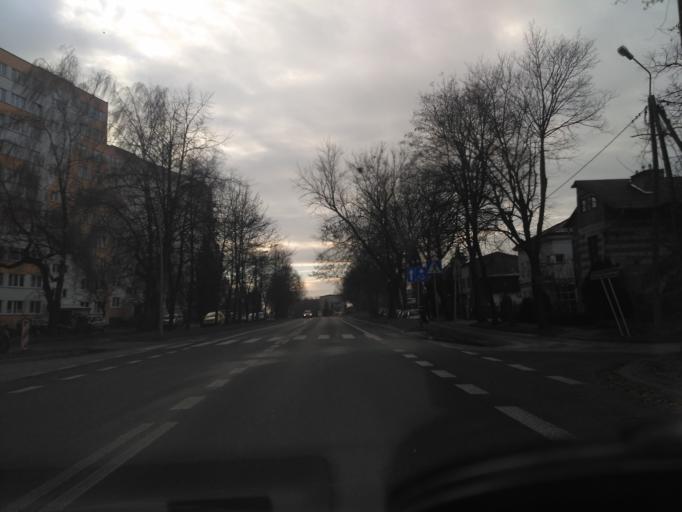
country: PL
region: Lublin Voivodeship
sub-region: Powiat lubelski
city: Lublin
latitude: 51.2655
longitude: 22.5421
